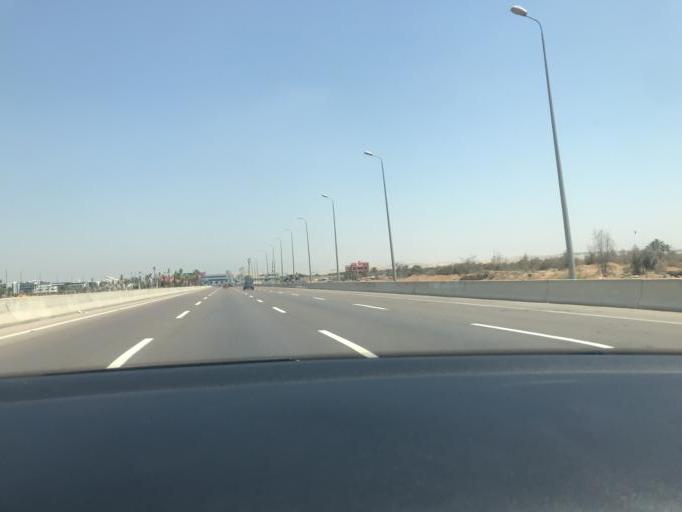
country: EG
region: Al Jizah
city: Awsim
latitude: 30.0734
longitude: 31.0073
